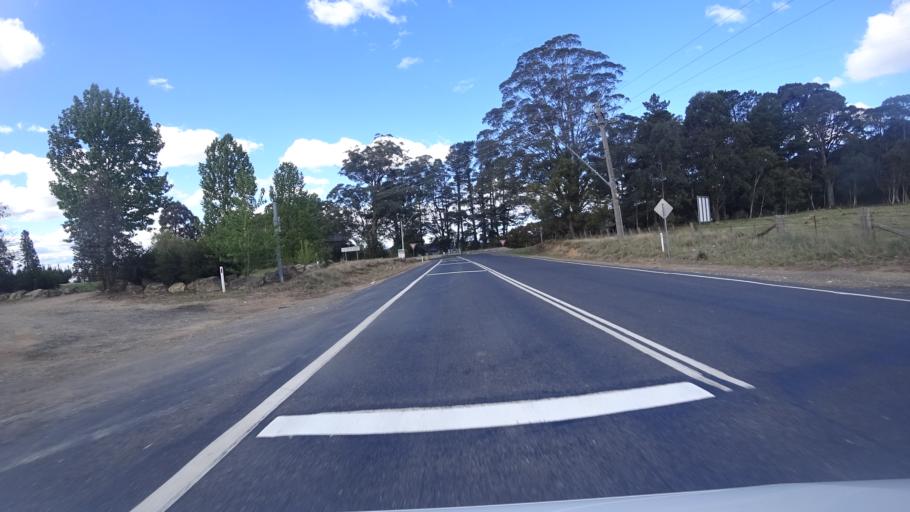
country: AU
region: New South Wales
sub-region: Lithgow
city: Bowenfels
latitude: -33.6774
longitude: 150.0500
